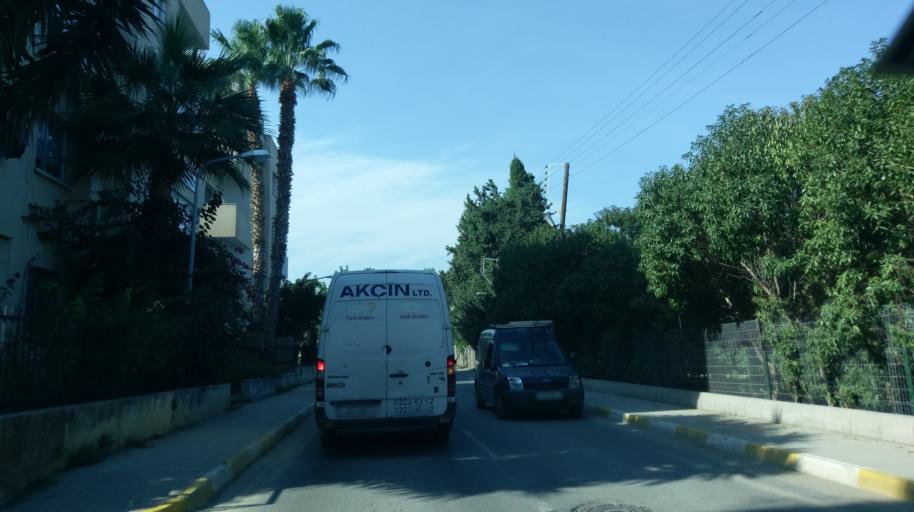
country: CY
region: Keryneia
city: Kyrenia
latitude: 35.3373
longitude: 33.3035
